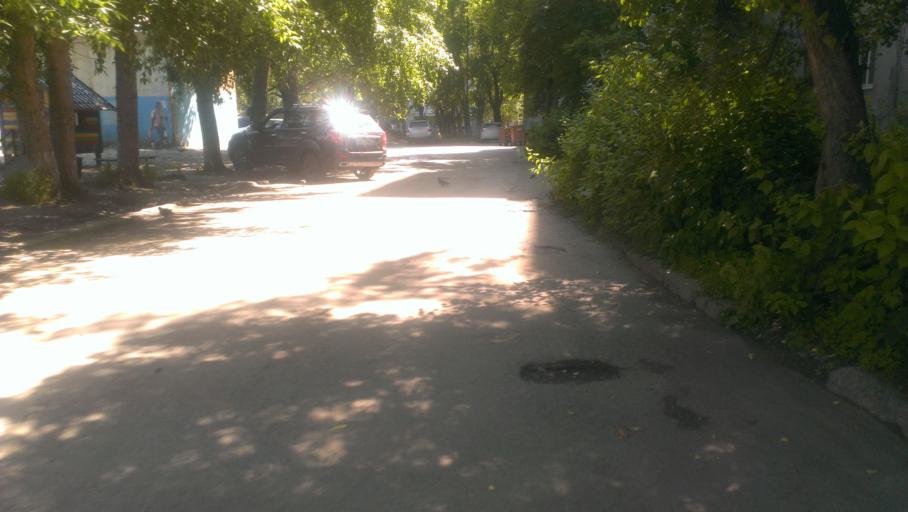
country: RU
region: Altai Krai
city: Novosilikatnyy
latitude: 53.3455
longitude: 83.6808
